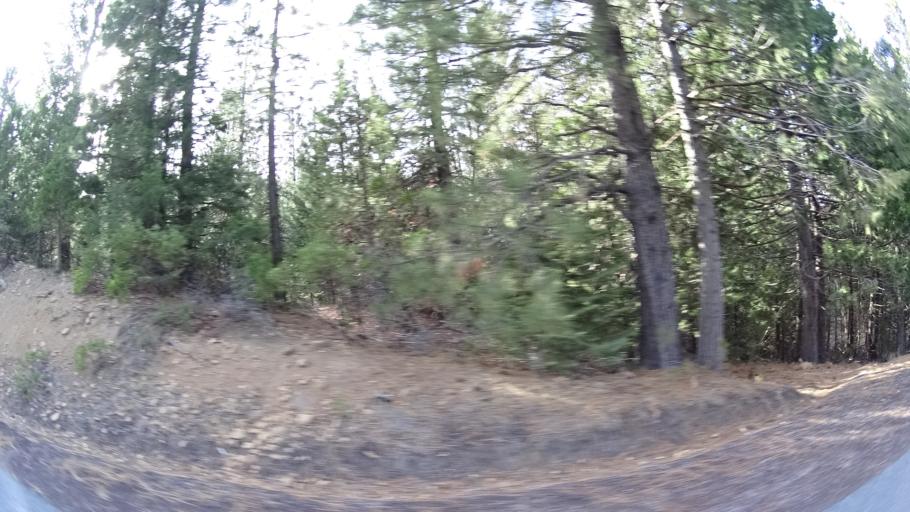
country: US
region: California
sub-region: Siskiyou County
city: Weed
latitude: 41.3917
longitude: -122.4127
